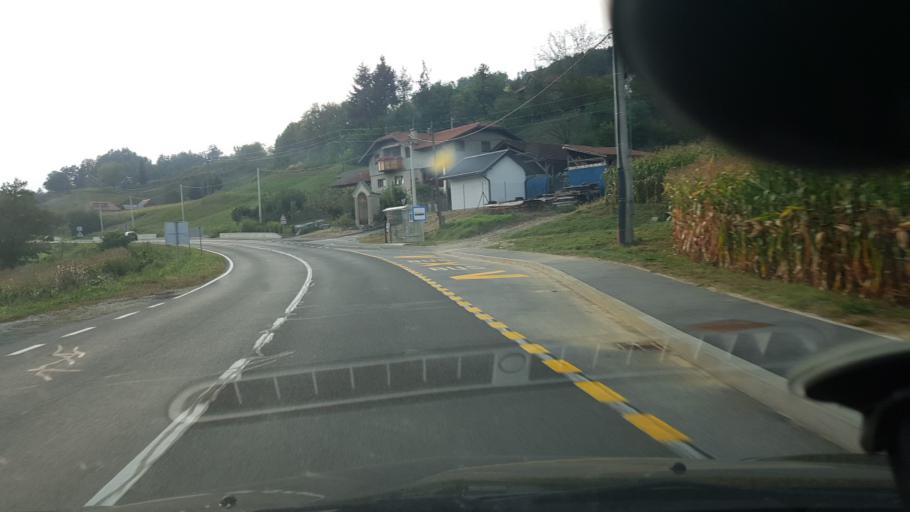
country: HR
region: Krapinsko-Zagorska
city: Pregrada
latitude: 46.2087
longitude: 15.7887
